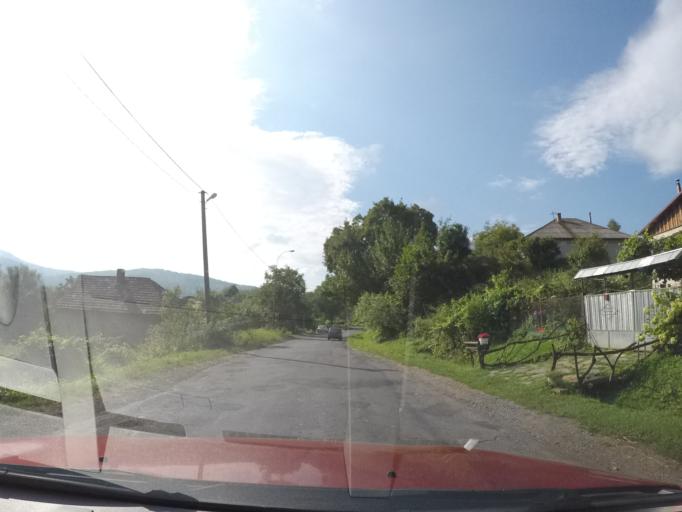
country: UA
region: Zakarpattia
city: Velykyi Bereznyi
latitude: 48.9141
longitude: 22.4596
